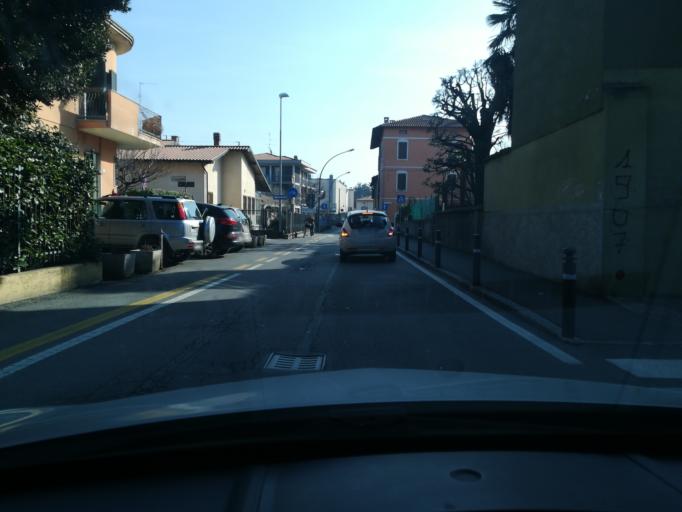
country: IT
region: Lombardy
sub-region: Provincia di Bergamo
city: Stezzano
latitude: 45.6535
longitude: 9.6517
